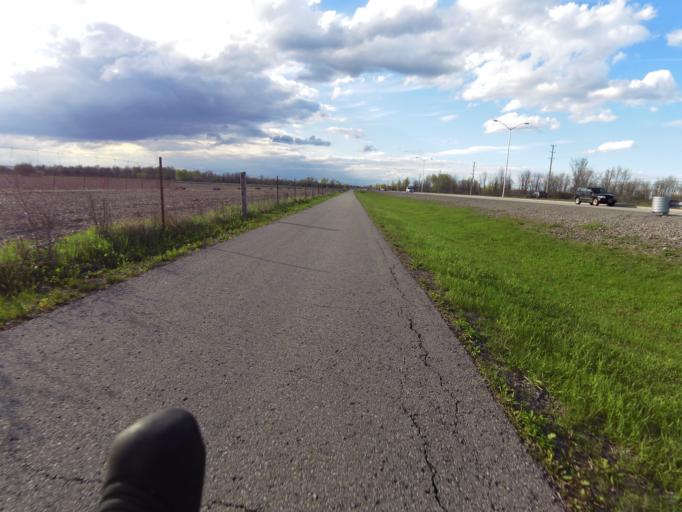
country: CA
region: Ontario
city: Ottawa
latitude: 45.3037
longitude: -75.6807
